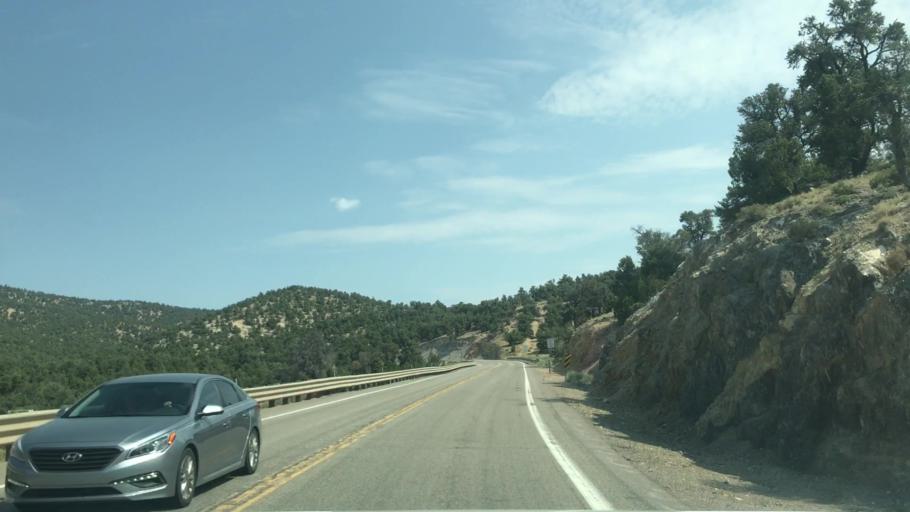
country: US
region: Nevada
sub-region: White Pine County
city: Ely
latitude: 39.0439
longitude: -114.6122
